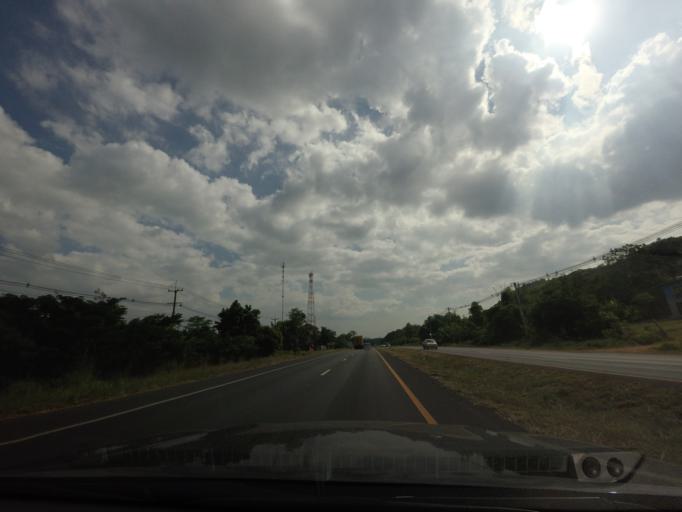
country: TH
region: Lop Buri
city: Chai Badan
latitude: 15.2901
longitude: 101.1273
